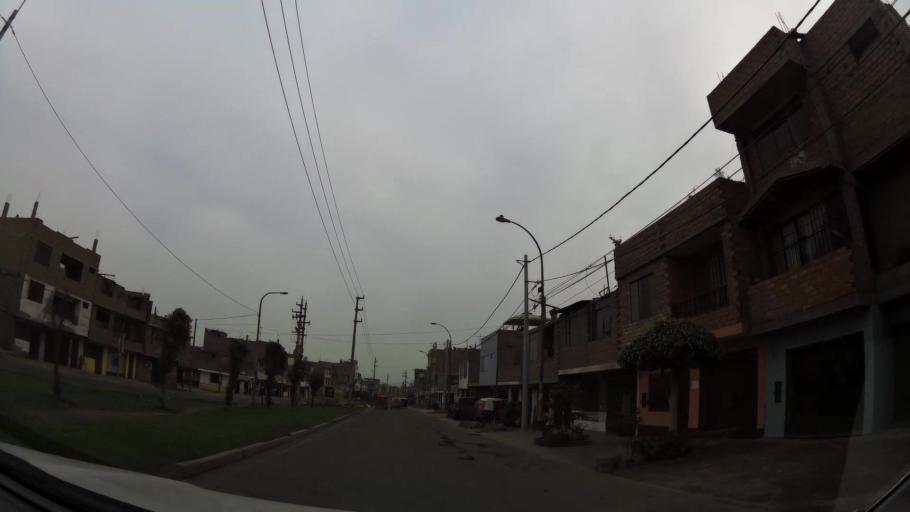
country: PE
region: Lima
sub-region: Lima
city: Independencia
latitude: -11.9597
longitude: -76.9913
